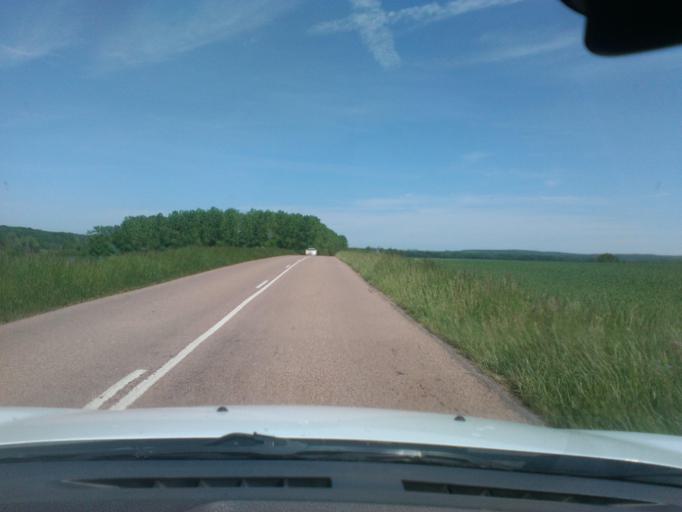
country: FR
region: Lorraine
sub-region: Departement des Vosges
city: Rambervillers
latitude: 48.4027
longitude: 6.5889
